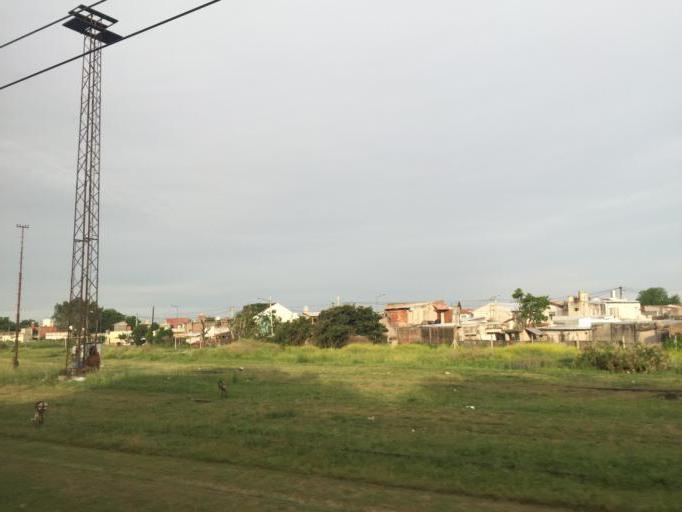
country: AR
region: Buenos Aires
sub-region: Partido de Lanus
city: Lanus
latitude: -34.6915
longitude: -58.3844
